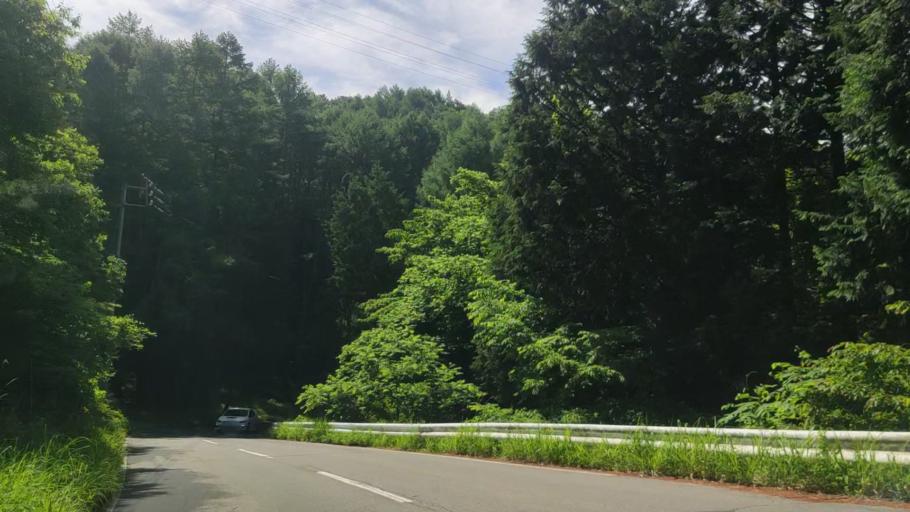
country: JP
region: Nagano
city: Suwa
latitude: 36.0723
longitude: 138.1374
